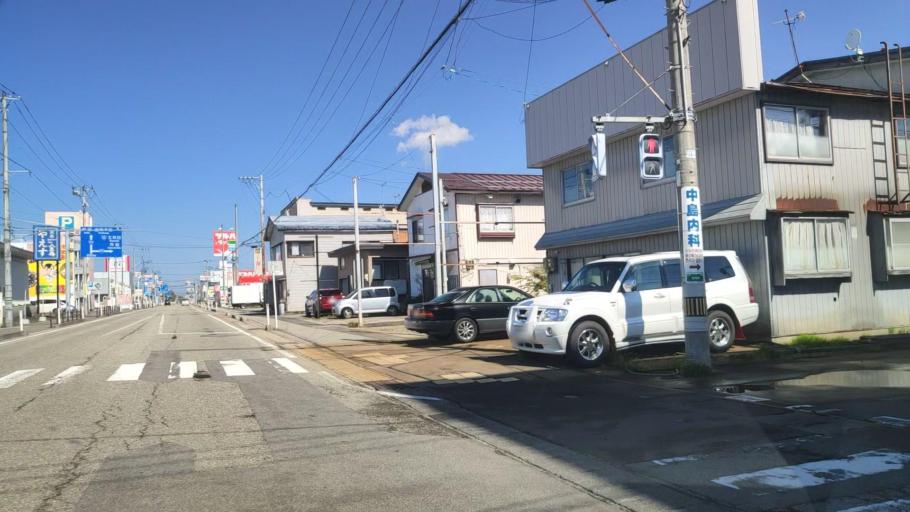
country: JP
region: Akita
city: Omagari
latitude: 39.4675
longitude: 140.4714
